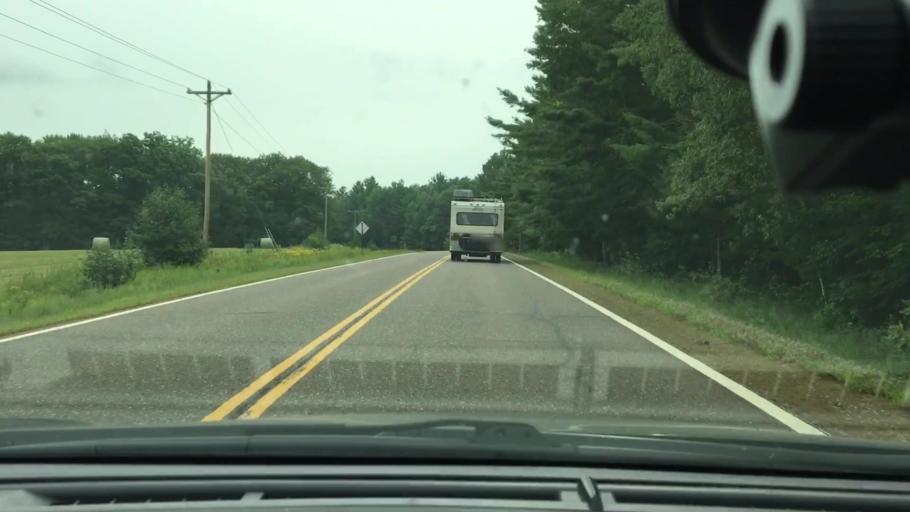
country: US
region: Minnesota
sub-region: Aitkin County
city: Aitkin
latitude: 46.4030
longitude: -93.8034
